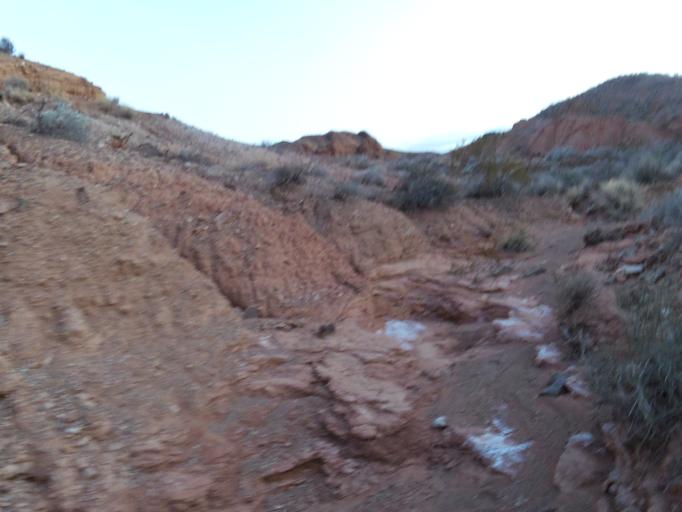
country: US
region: Nevada
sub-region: Clark County
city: Boulder City
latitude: 36.2397
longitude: -114.6279
